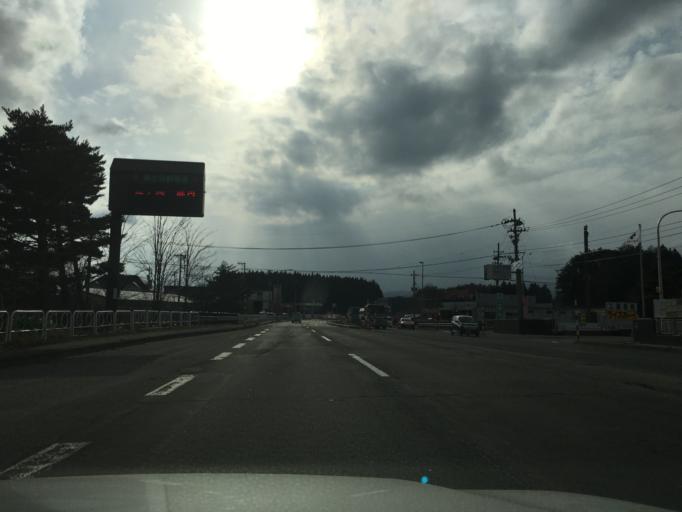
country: JP
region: Aomori
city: Aomori Shi
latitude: 40.8336
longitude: 140.6710
